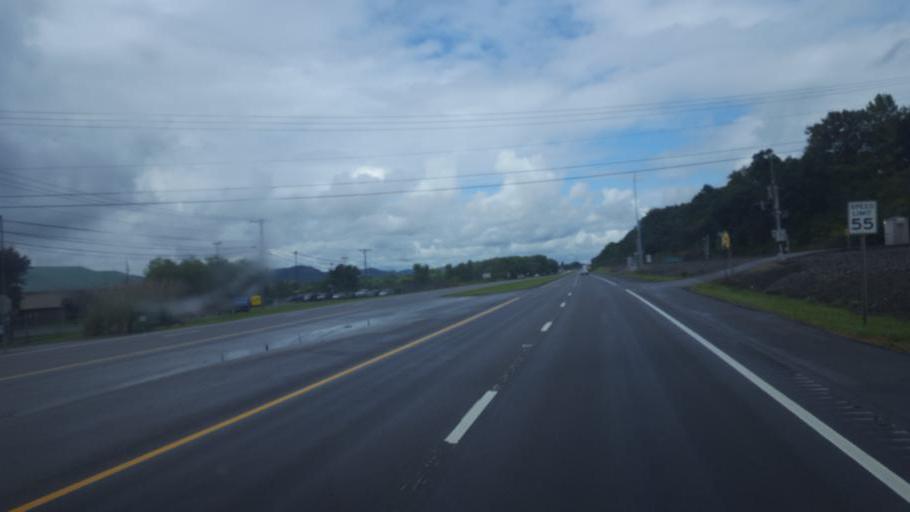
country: US
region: Ohio
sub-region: Scioto County
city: Lucasville
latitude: 38.8597
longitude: -82.9890
